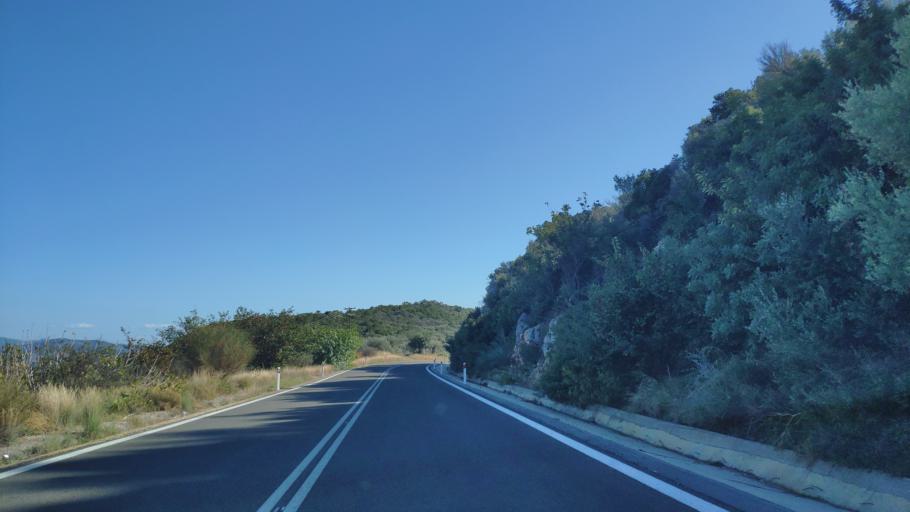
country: GR
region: Peloponnese
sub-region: Nomos Argolidos
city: Palaia Epidavros
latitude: 37.5630
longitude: 23.2552
